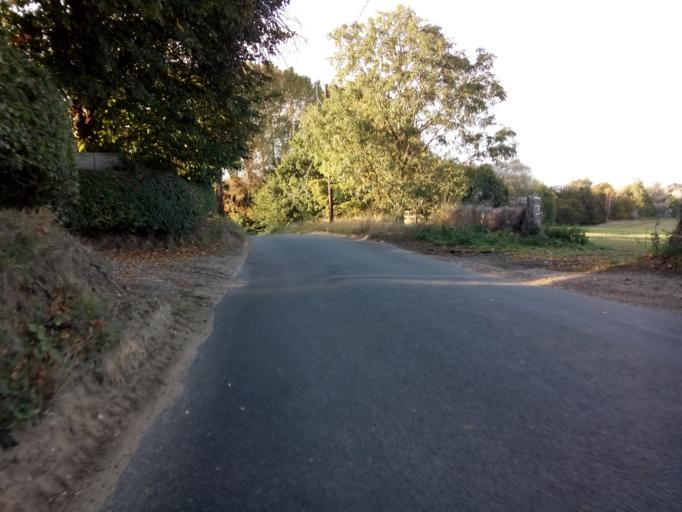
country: GB
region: England
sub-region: Suffolk
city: Bramford
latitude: 52.0301
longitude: 1.0927
